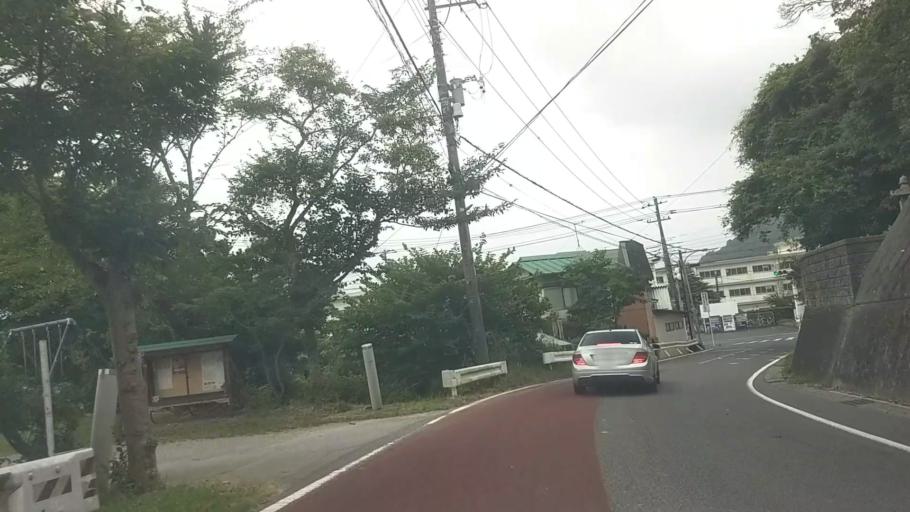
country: JP
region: Chiba
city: Futtsu
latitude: 35.2183
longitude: 139.8796
